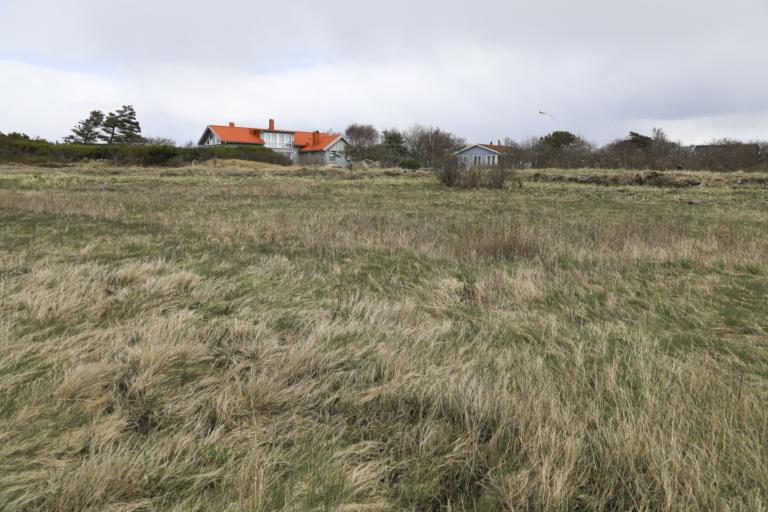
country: SE
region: Halland
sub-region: Varbergs Kommun
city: Traslovslage
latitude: 57.0748
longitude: 12.2608
